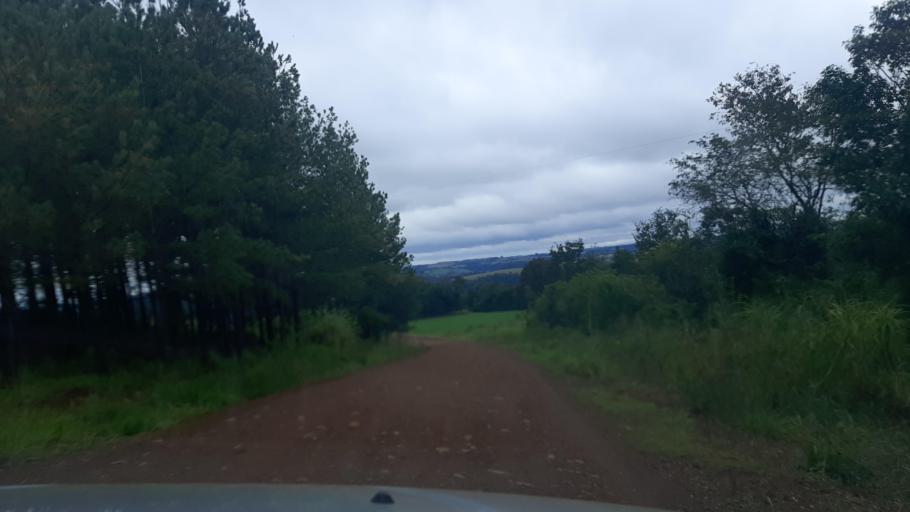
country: BR
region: Parana
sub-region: Ampere
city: Ampere
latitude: -26.0500
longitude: -53.5546
